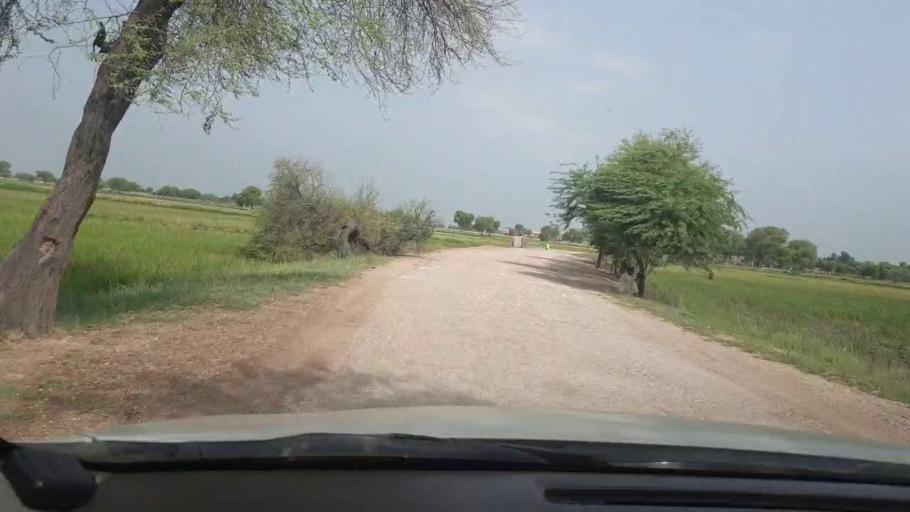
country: PK
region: Sindh
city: Shikarpur
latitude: 28.0009
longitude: 68.5944
